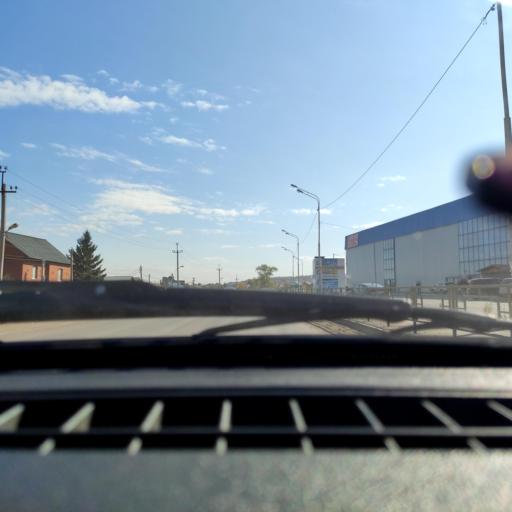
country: RU
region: Bashkortostan
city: Ufa
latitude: 54.6175
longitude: 55.9311
